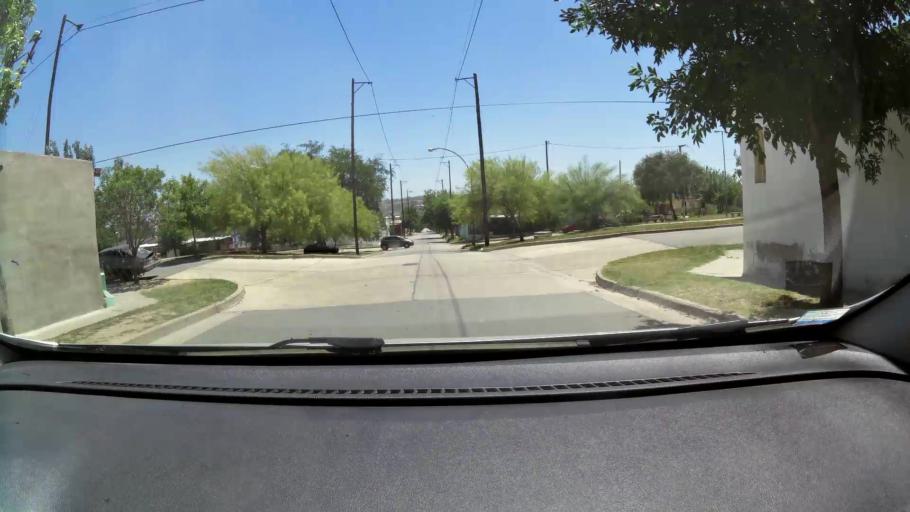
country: AR
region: Cordoba
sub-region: Departamento de Capital
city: Cordoba
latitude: -31.4194
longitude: -64.1183
